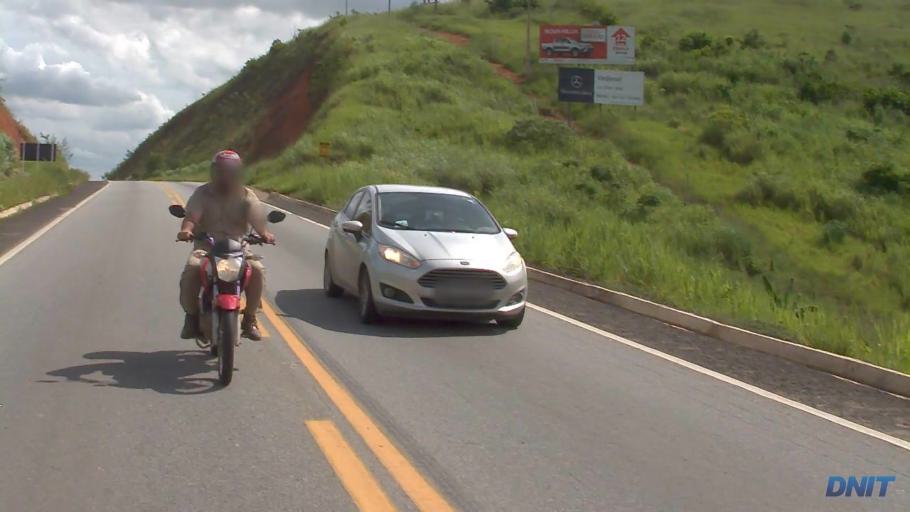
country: BR
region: Minas Gerais
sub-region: Ipatinga
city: Ipatinga
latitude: -19.4171
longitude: -42.4927
